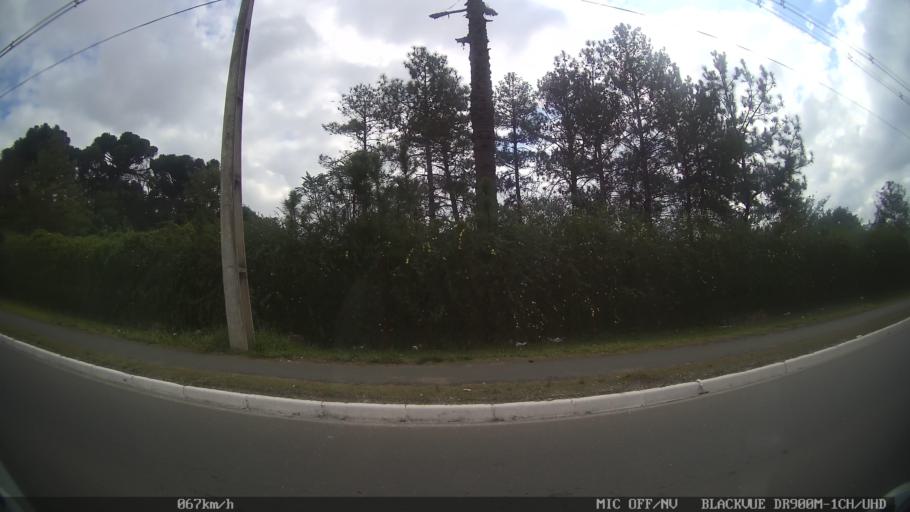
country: BR
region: Parana
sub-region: Pinhais
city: Pinhais
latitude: -25.3826
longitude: -49.2008
